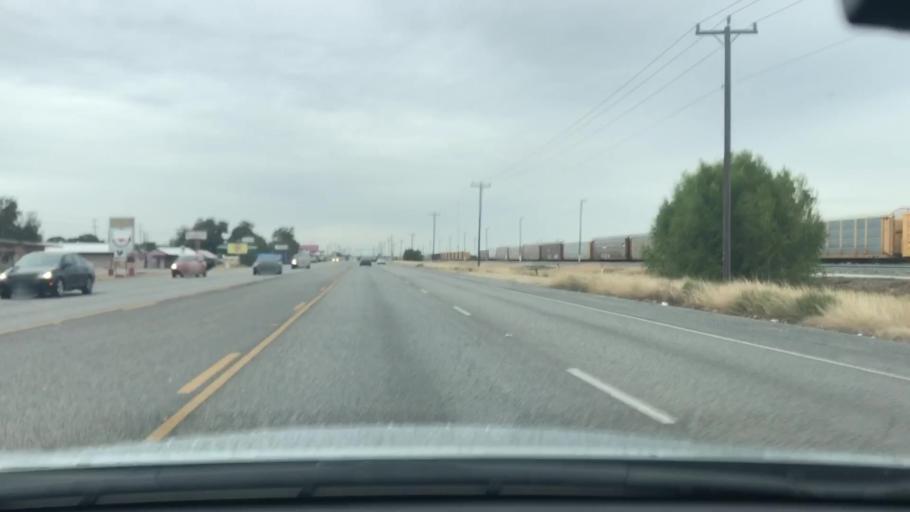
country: US
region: Texas
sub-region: Bexar County
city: Kirby
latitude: 29.4669
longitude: -98.3936
